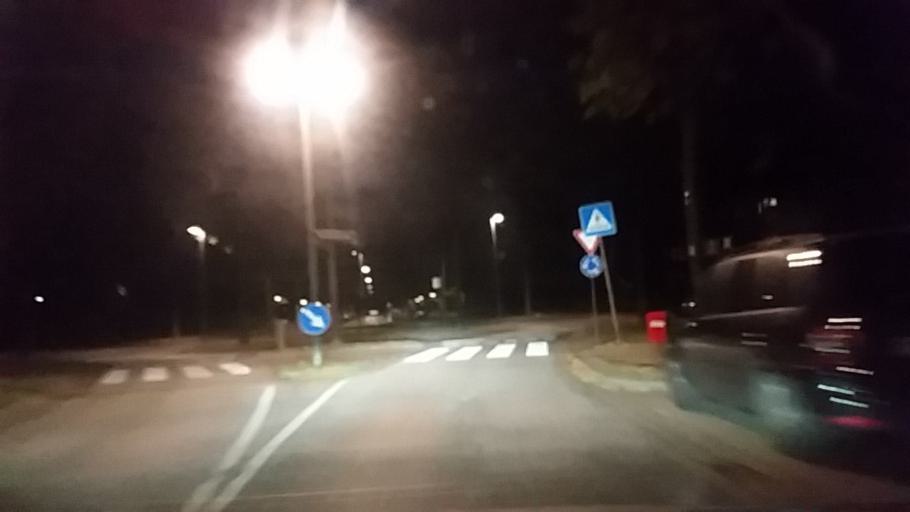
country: DE
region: Schleswig-Holstein
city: Oststeinbek
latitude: 53.5294
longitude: 10.1499
